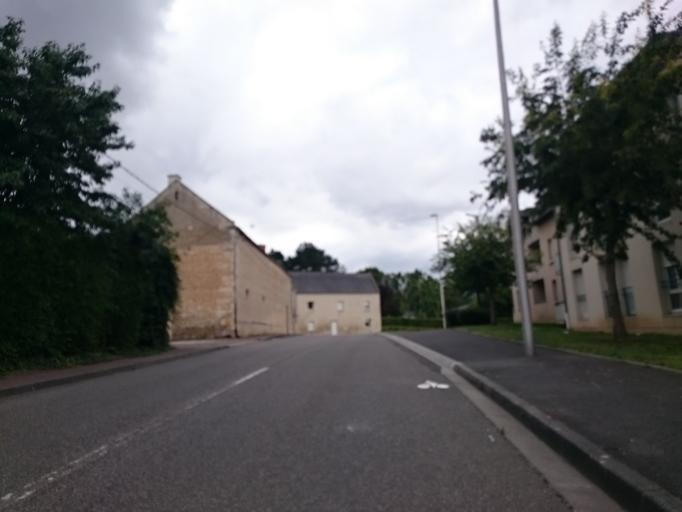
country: FR
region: Lower Normandy
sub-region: Departement du Calvados
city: Fleury-sur-Orne
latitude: 49.1429
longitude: -0.3836
